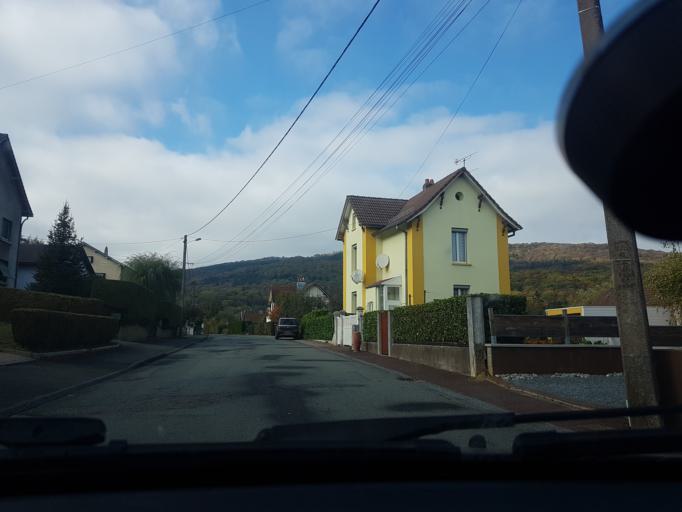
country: FR
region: Franche-Comte
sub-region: Territoire de Belfort
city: Cravanche
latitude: 47.6506
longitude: 6.8312
